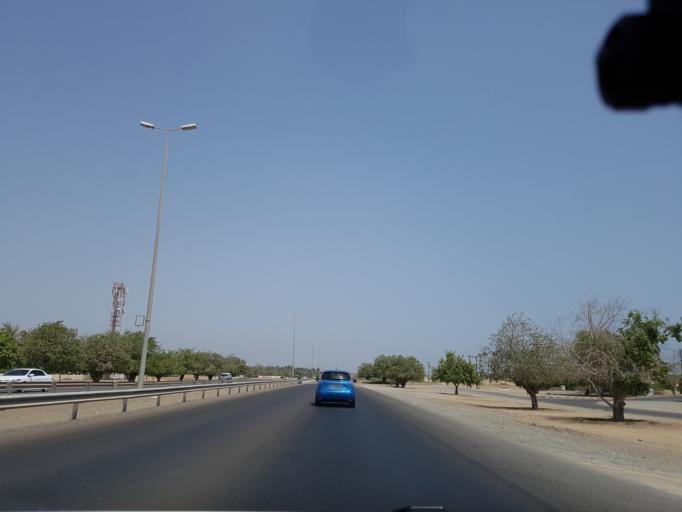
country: OM
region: Al Batinah
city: Saham
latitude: 24.1728
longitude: 56.8593
